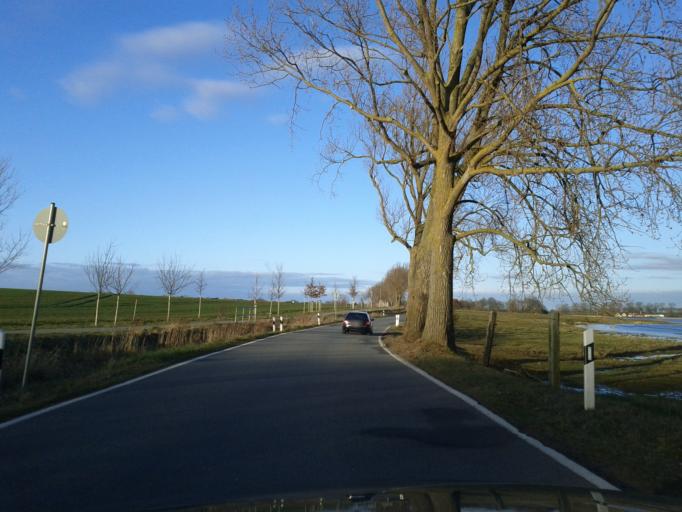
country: DE
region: Mecklenburg-Vorpommern
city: Wismar
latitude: 53.9873
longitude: 11.4280
